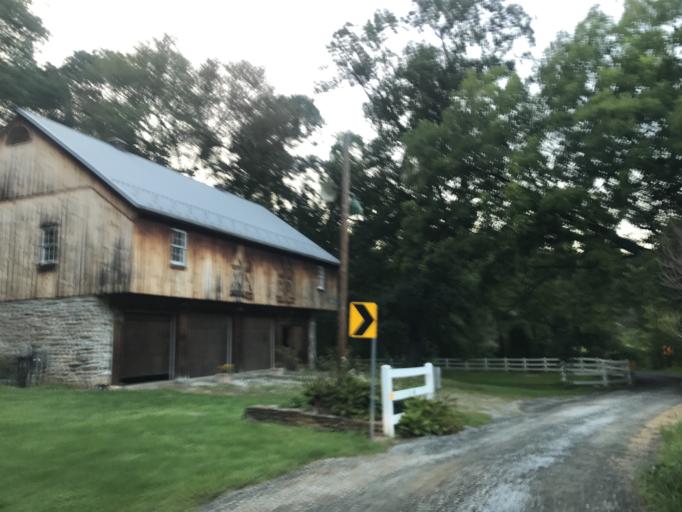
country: US
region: Maryland
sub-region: Harford County
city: Jarrettsville
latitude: 39.6742
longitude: -76.5363
